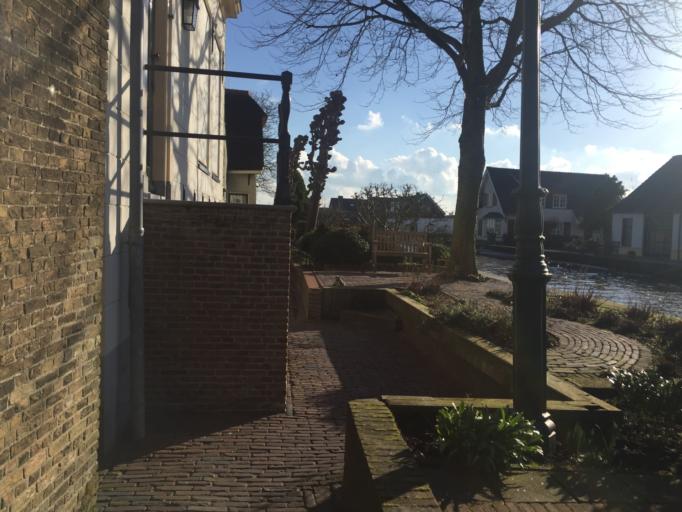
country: NL
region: South Holland
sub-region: Gemeente Vlist
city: Haastrecht
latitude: 52.0443
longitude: 4.8011
